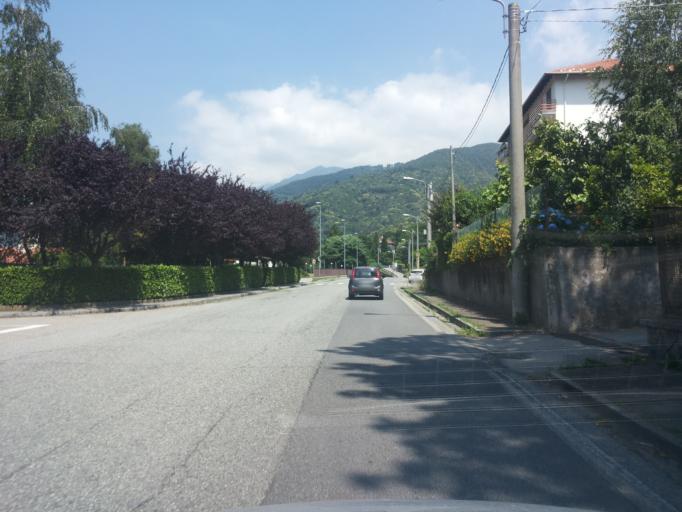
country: IT
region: Piedmont
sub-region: Provincia di Biella
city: Sagliano Micca
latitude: 45.6234
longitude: 8.0456
